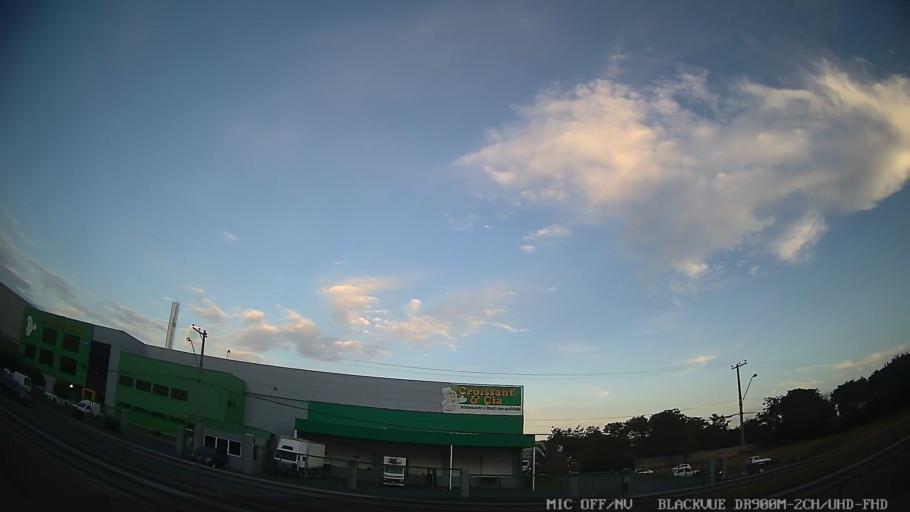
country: BR
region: Sao Paulo
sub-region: Indaiatuba
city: Indaiatuba
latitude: -23.1354
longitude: -47.2395
